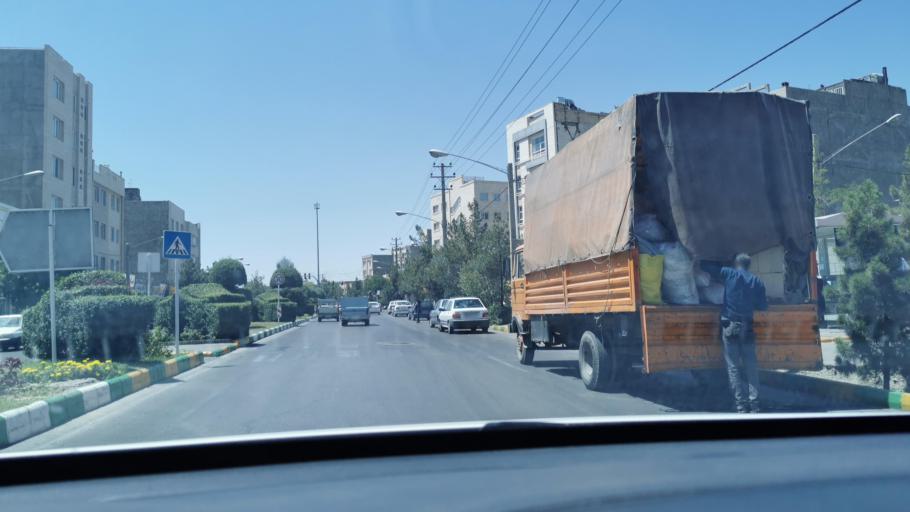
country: IR
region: Razavi Khorasan
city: Mashhad
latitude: 36.3395
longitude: 59.4847
